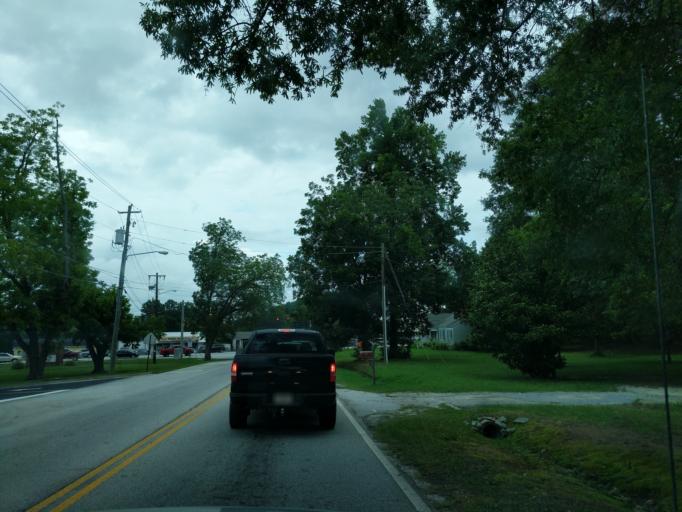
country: US
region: Georgia
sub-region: Walton County
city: Loganville
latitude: 33.8410
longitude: -83.8969
